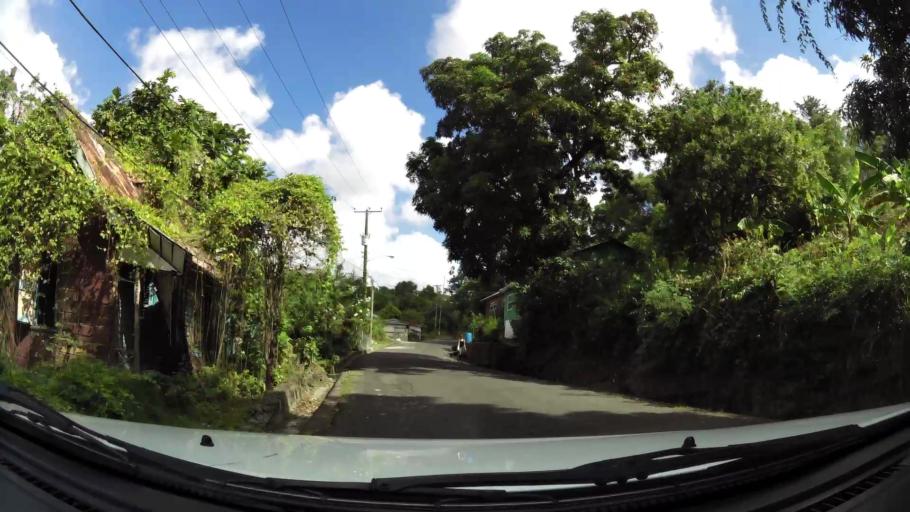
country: LC
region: Laborie Quarter
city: Laborie
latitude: 13.7513
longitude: -60.9915
